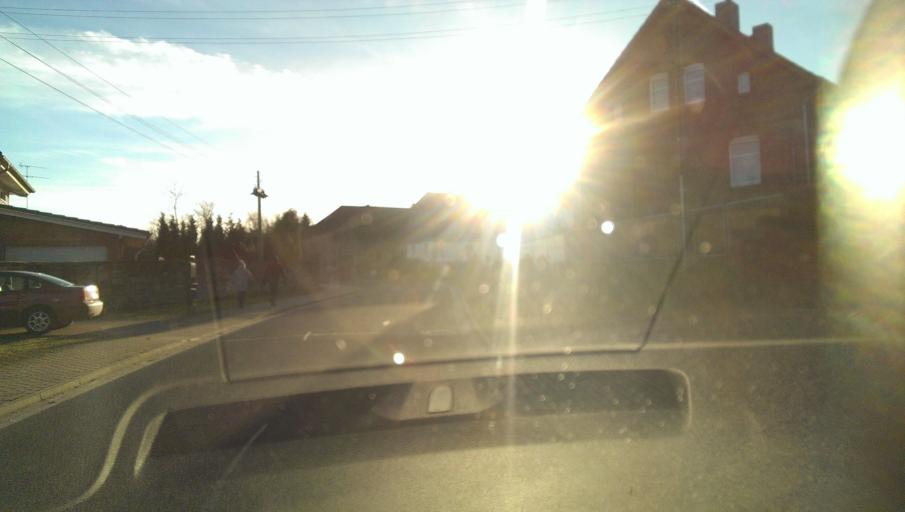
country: DE
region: Saxony-Anhalt
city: Eilsleben
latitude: 52.1346
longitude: 11.1912
